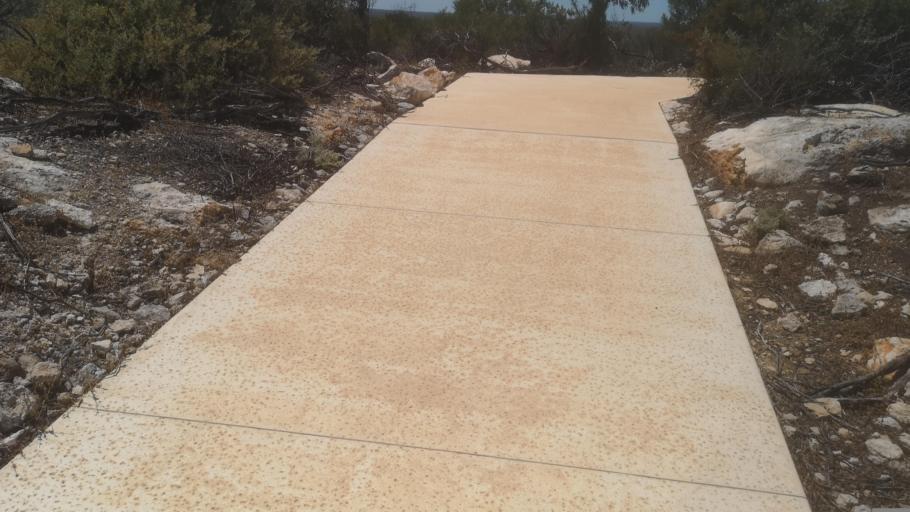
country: AU
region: Western Australia
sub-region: Northampton Shire
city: Kalbarri
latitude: -27.6978
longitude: 114.2170
